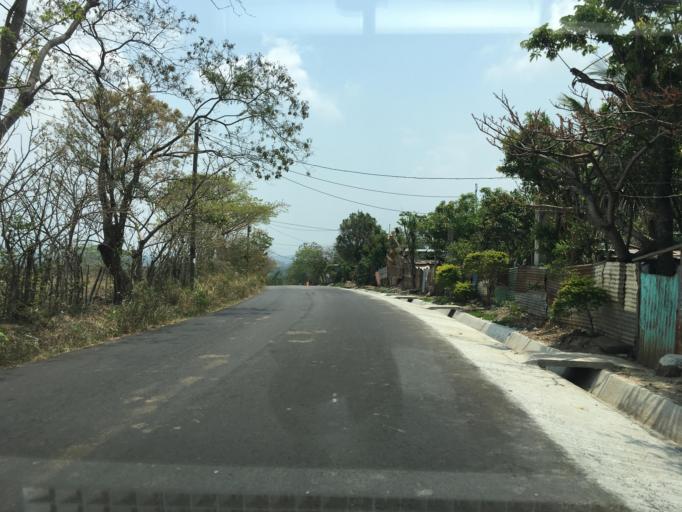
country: GT
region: Santa Rosa
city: Pueblo Nuevo Vinas
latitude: 14.3145
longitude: -90.5465
